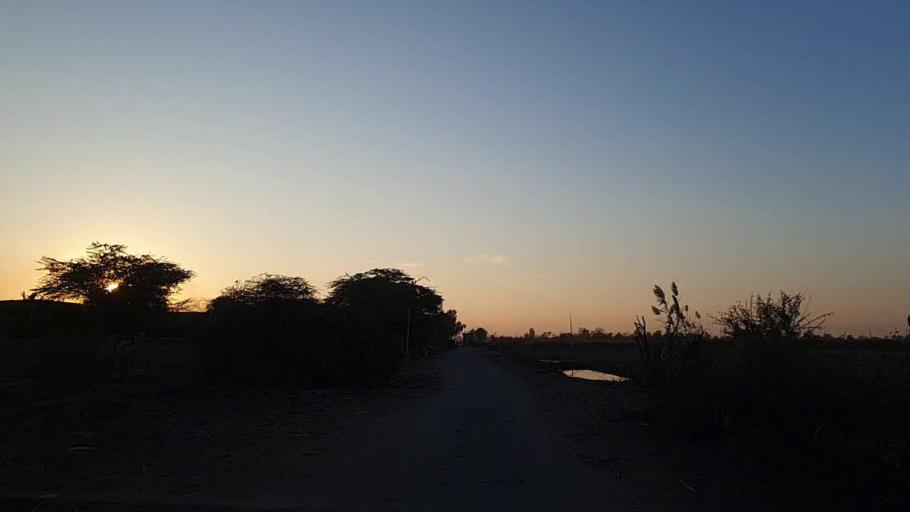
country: PK
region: Sindh
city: Bandhi
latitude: 26.6201
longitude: 68.3620
